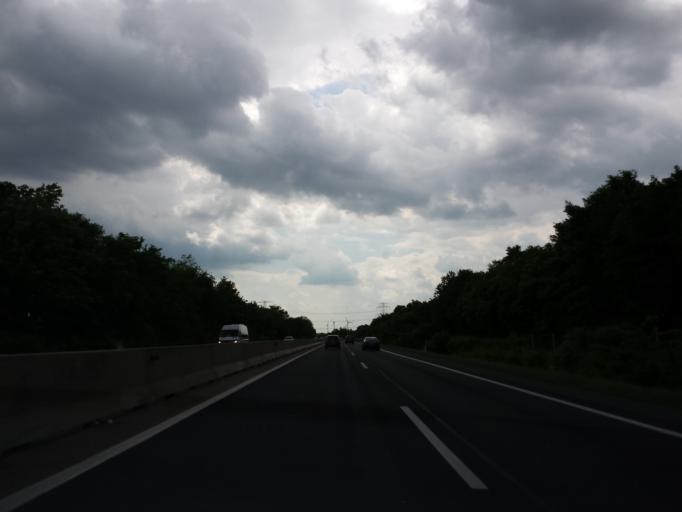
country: AT
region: Lower Austria
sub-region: Politischer Bezirk Ganserndorf
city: Orth an der Donau
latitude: 48.0820
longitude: 16.6753
